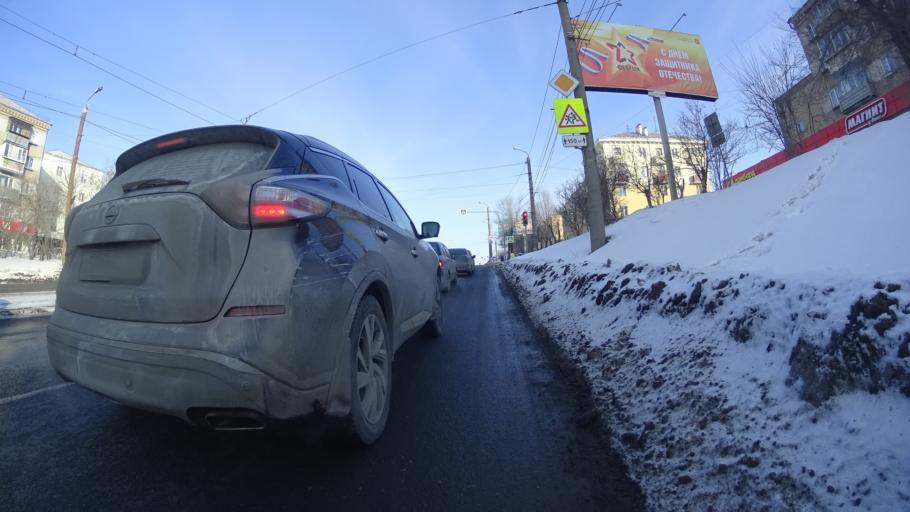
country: RU
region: Chelyabinsk
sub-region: Gorod Chelyabinsk
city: Chelyabinsk
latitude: 55.1853
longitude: 61.4197
